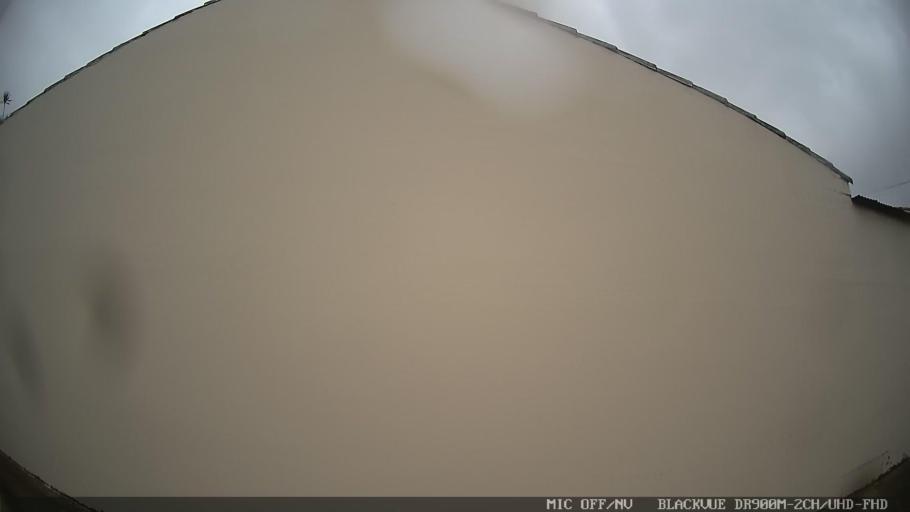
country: BR
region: Sao Paulo
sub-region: Itanhaem
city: Itanhaem
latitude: -24.1746
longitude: -46.7752
